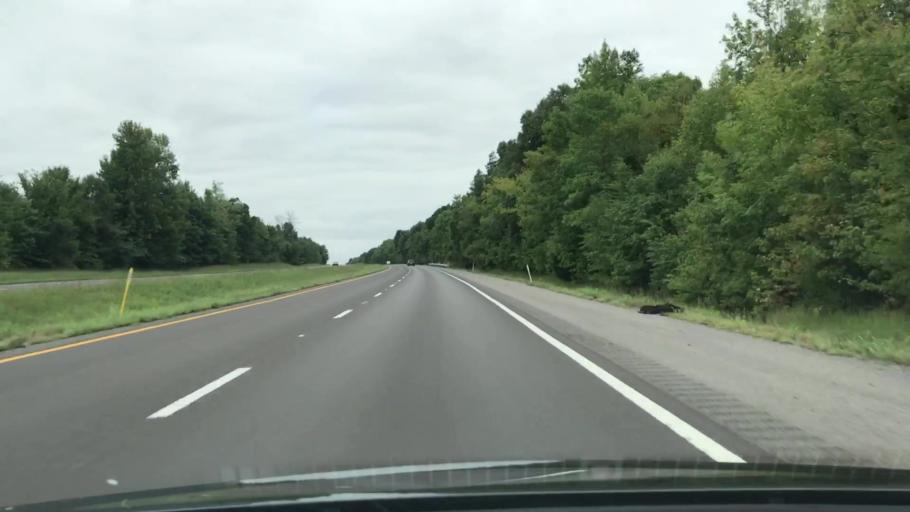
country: US
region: Kentucky
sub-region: Graves County
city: Mayfield
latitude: 36.6818
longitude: -88.7325
